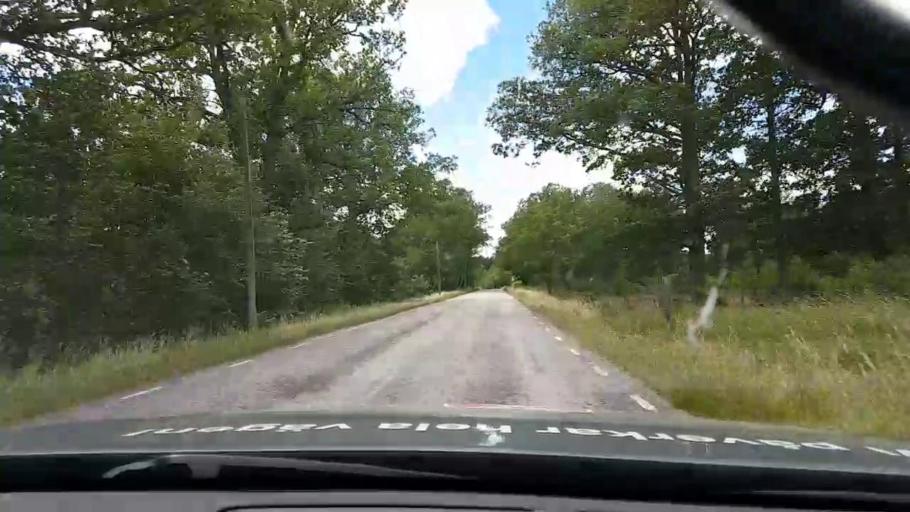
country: SE
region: Kalmar
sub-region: Vasterviks Kommun
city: Forserum
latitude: 58.0186
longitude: 16.5204
